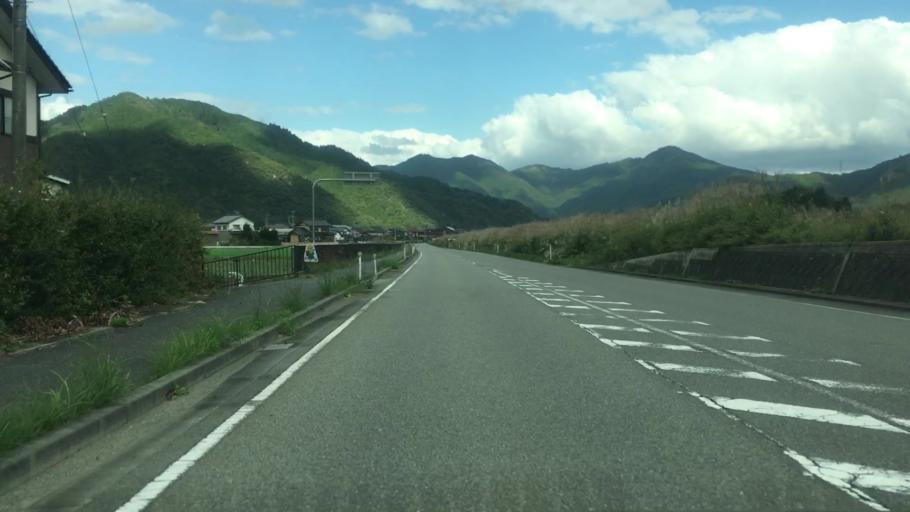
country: JP
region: Hyogo
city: Toyooka
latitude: 35.3745
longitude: 134.7679
